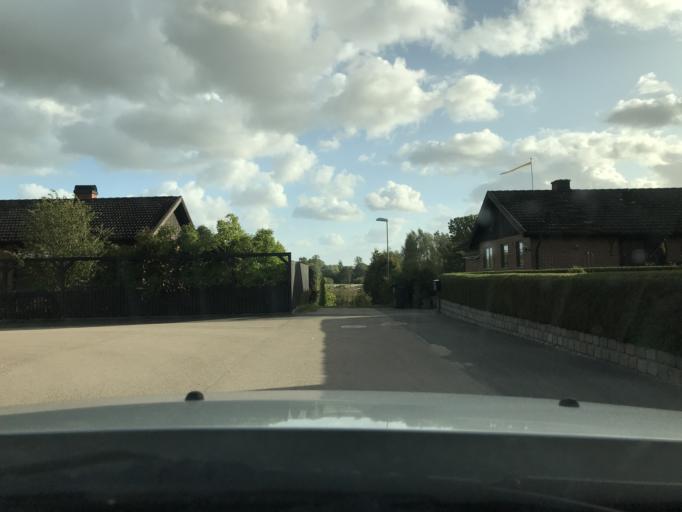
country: SE
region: Skane
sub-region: Eslovs Kommun
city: Eslov
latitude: 55.7523
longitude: 13.3584
